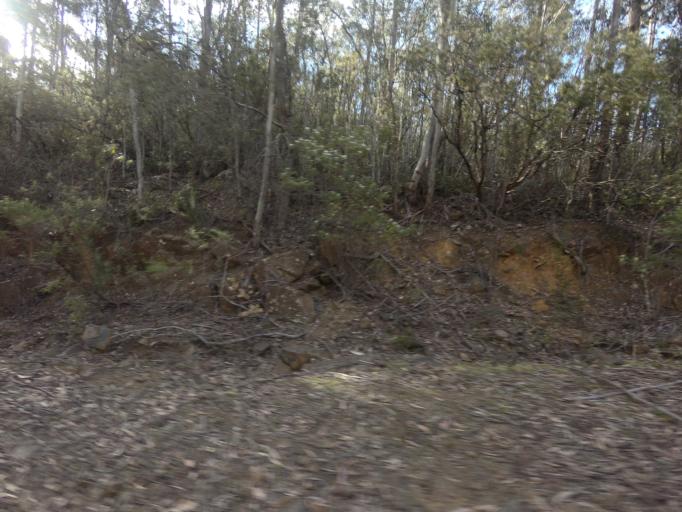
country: AU
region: Tasmania
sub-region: Break O'Day
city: St Helens
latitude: -41.8509
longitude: 148.0465
